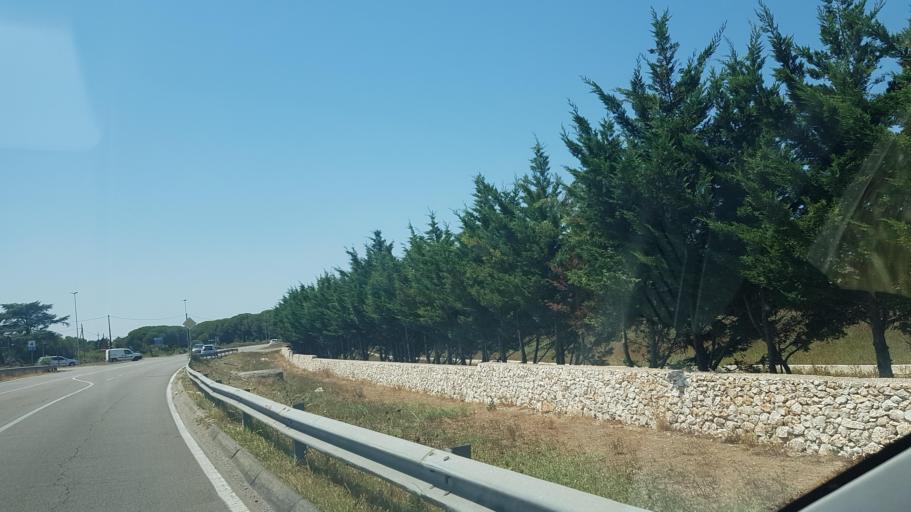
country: IT
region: Apulia
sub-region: Provincia di Lecce
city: Melendugno
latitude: 40.2781
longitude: 18.3390
